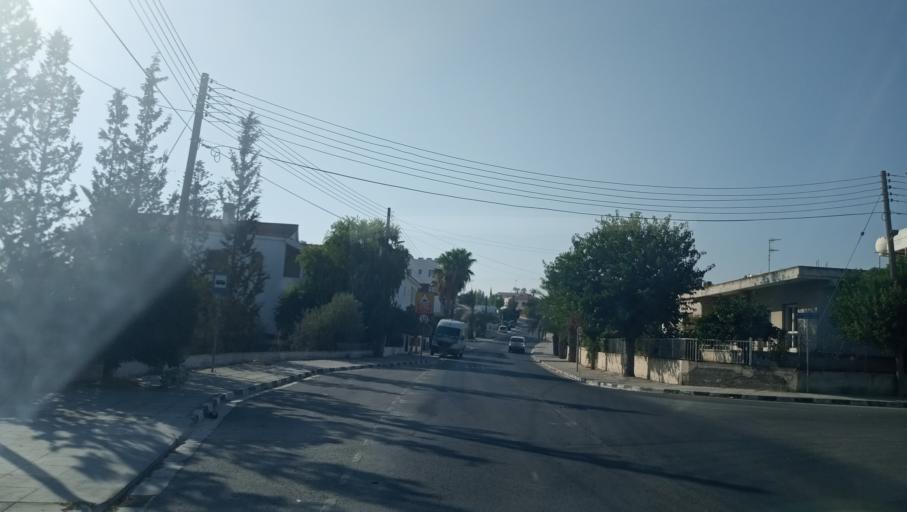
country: CY
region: Lefkosia
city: Geri
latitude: 35.1136
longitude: 33.4212
